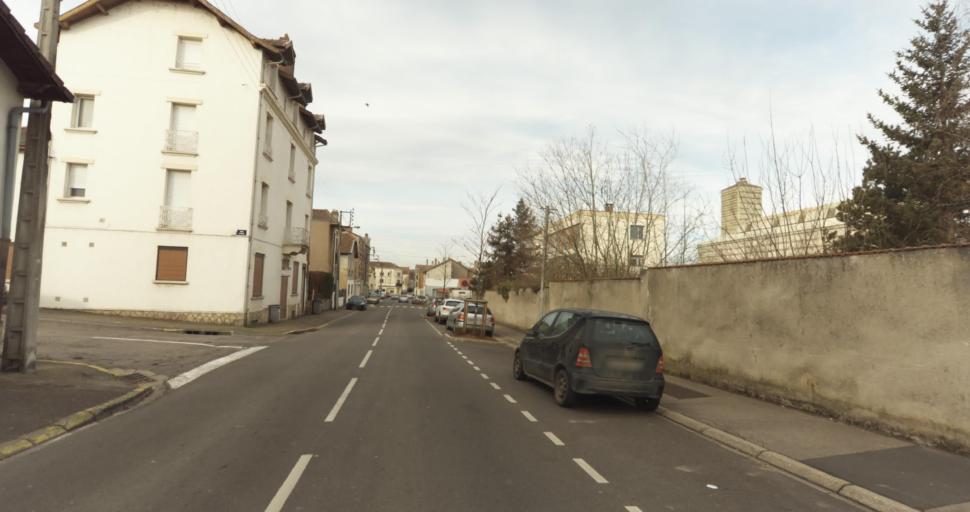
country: FR
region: Lorraine
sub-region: Departement de Meurthe-et-Moselle
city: Jarny
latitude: 49.1650
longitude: 5.8711
